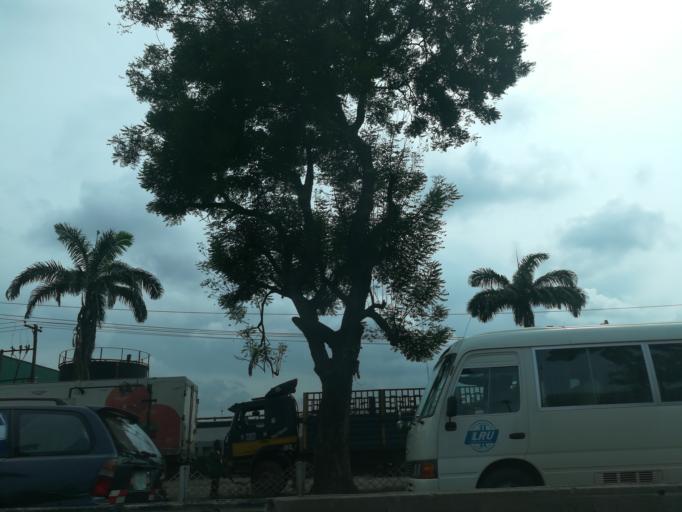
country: NG
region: Lagos
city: Ojota
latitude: 6.6022
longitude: 3.3733
